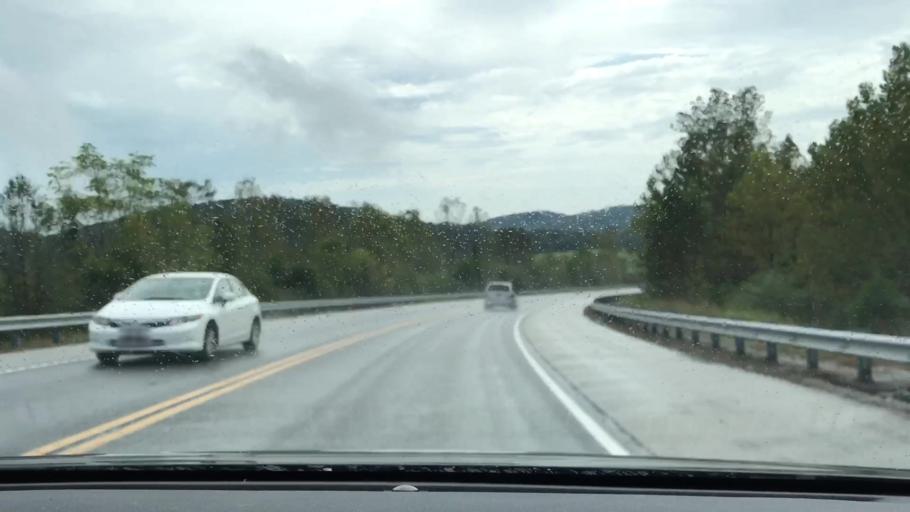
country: US
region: Tennessee
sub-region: Smith County
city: Carthage
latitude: 36.2586
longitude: -85.9342
